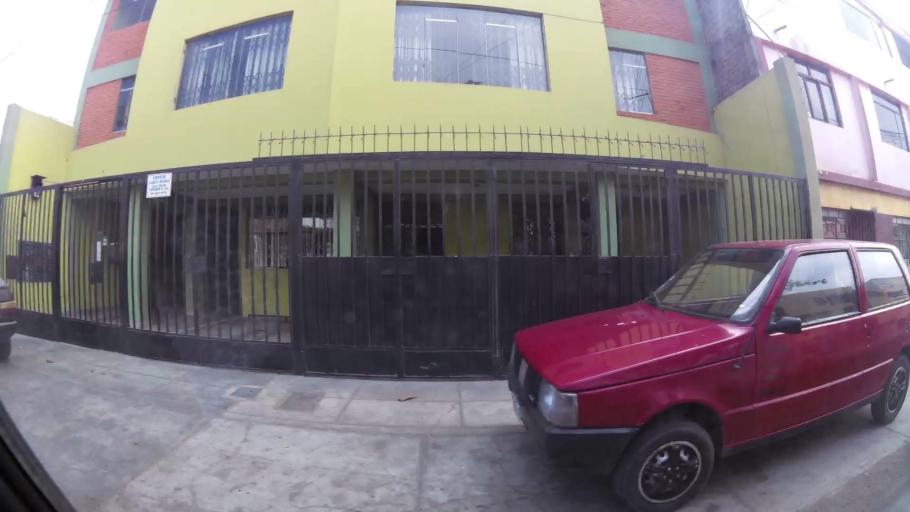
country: PE
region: La Libertad
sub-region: Provincia de Trujillo
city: Trujillo
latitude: -8.1213
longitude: -79.0222
